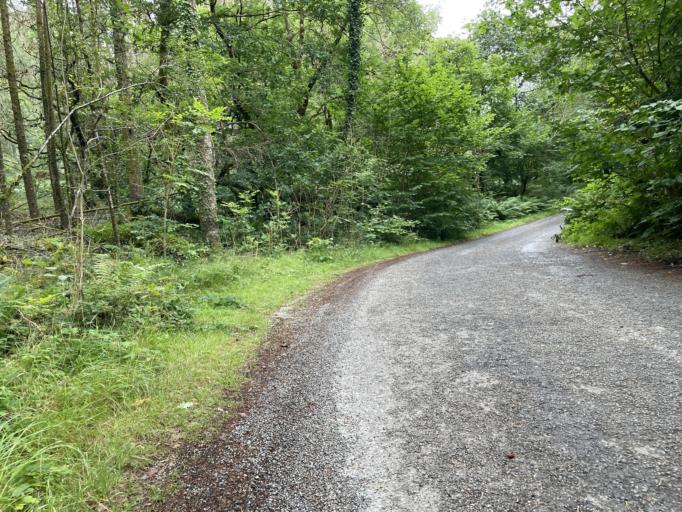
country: GB
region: Scotland
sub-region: Dumfries and Galloway
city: Newton Stewart
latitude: 55.0908
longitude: -4.4986
